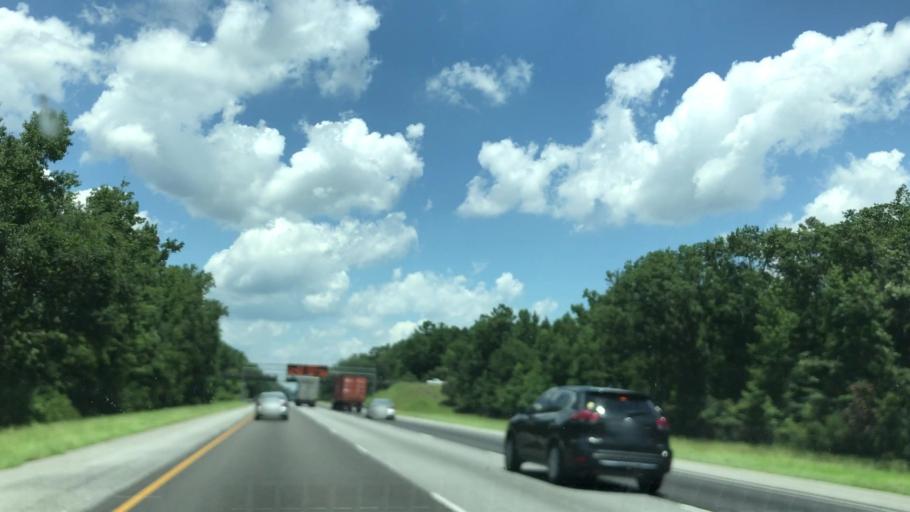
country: US
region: Georgia
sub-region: Liberty County
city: Midway
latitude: 31.6935
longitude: -81.3910
